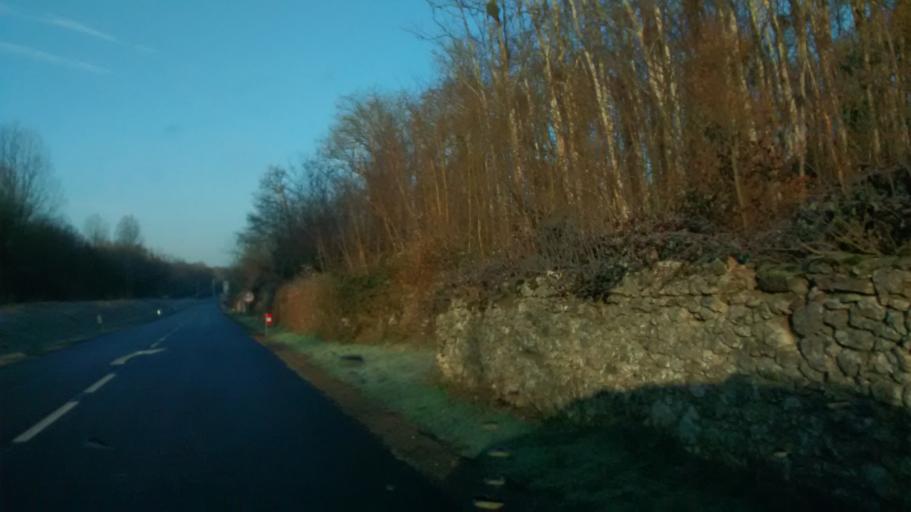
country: FR
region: Centre
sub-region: Departement d'Indre-et-Loire
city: Veigne
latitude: 47.2897
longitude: 0.7567
